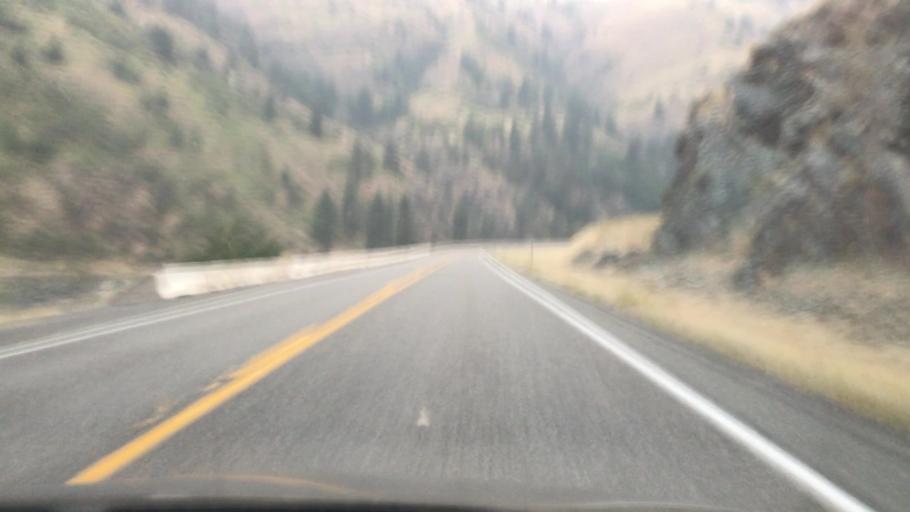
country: US
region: Idaho
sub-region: Idaho County
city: Grangeville
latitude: 45.6220
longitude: -116.2976
